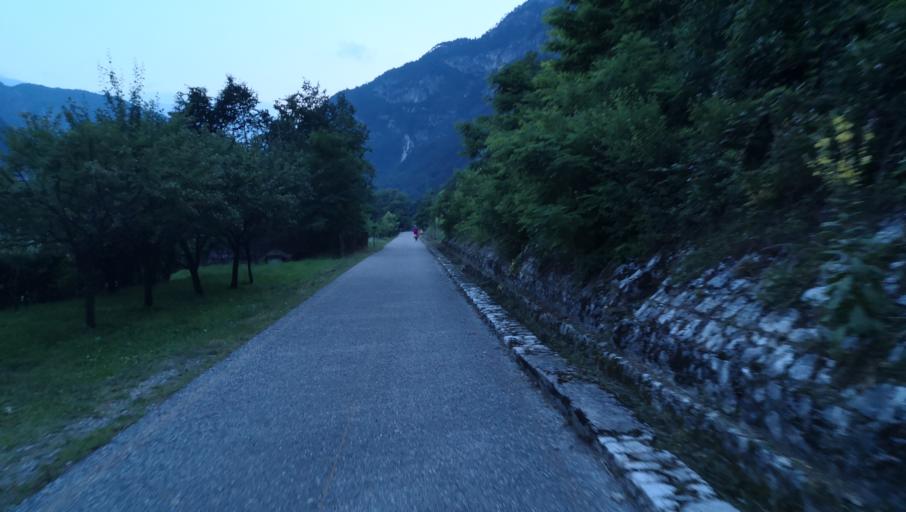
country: IT
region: Friuli Venezia Giulia
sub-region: Provincia di Udine
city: Chiusaforte
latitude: 46.4065
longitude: 13.3004
